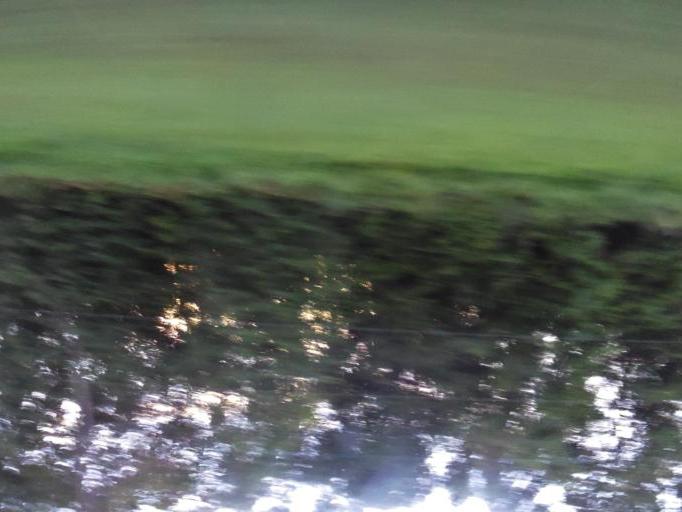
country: US
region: Georgia
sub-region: Camden County
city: Kingsland
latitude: 30.8466
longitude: -81.6996
